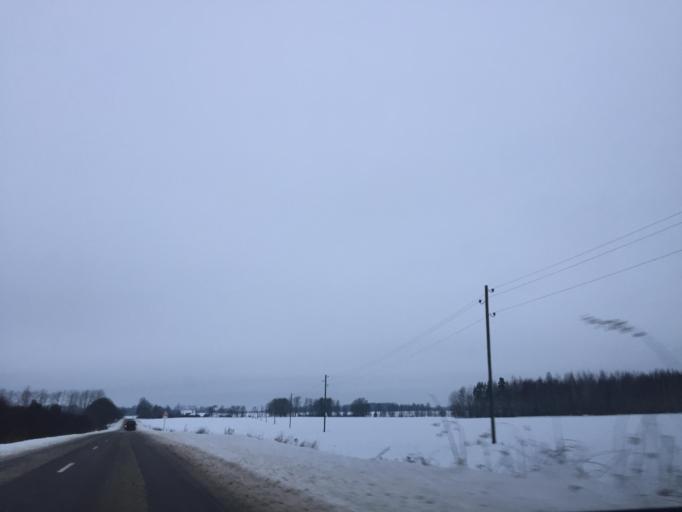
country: LV
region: Smiltene
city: Smiltene
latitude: 57.4293
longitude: 25.8418
